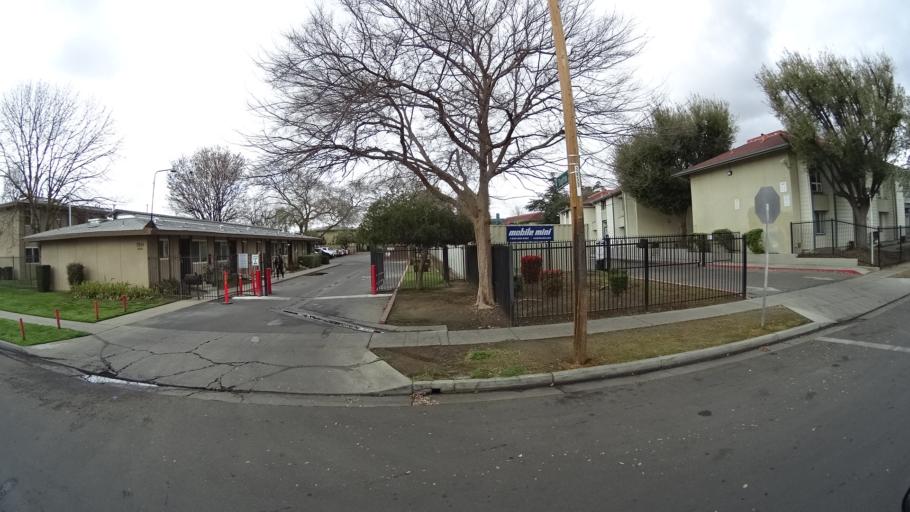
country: US
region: California
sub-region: Fresno County
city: West Park
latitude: 36.7829
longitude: -119.8400
